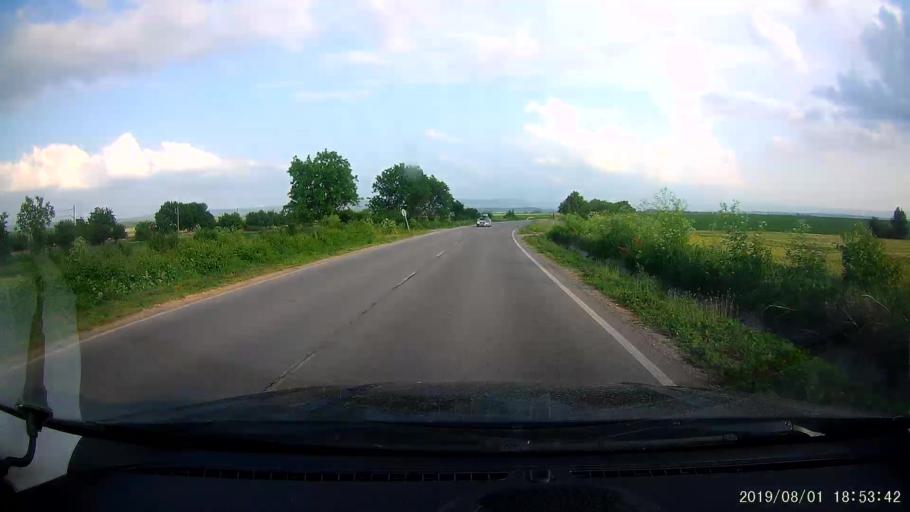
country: BG
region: Shumen
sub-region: Obshtina Shumen
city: Shumen
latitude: 43.2165
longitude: 26.9969
